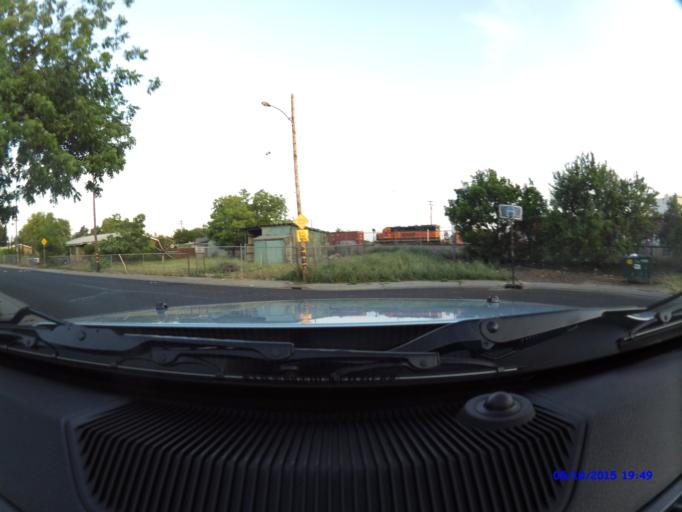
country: US
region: California
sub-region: San Joaquin County
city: Kennedy
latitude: 37.9512
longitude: -121.2519
